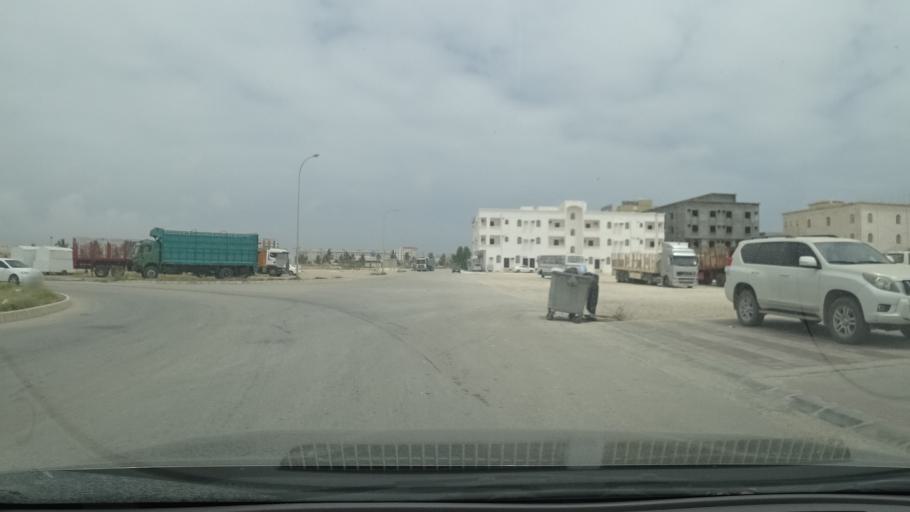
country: OM
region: Zufar
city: Salalah
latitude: 17.0264
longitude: 54.0553
